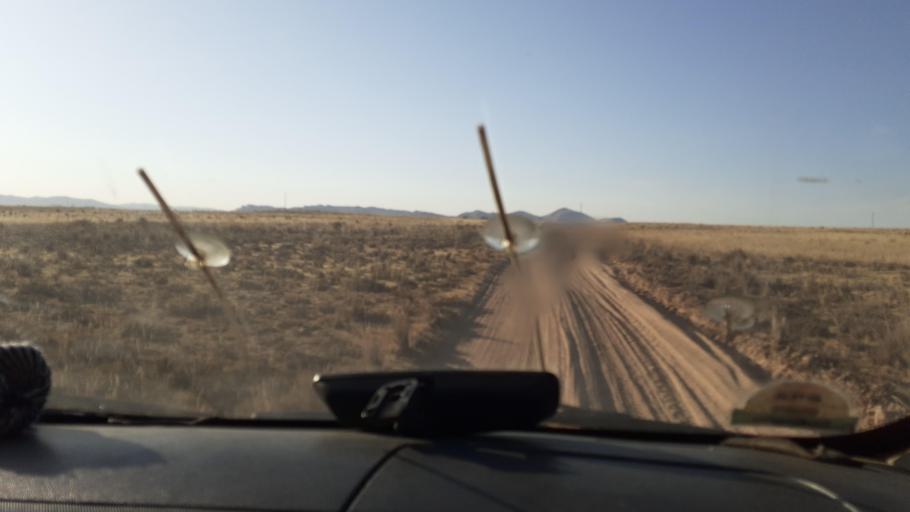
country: BO
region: La Paz
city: Tiahuanaco
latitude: -16.9749
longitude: -68.7451
